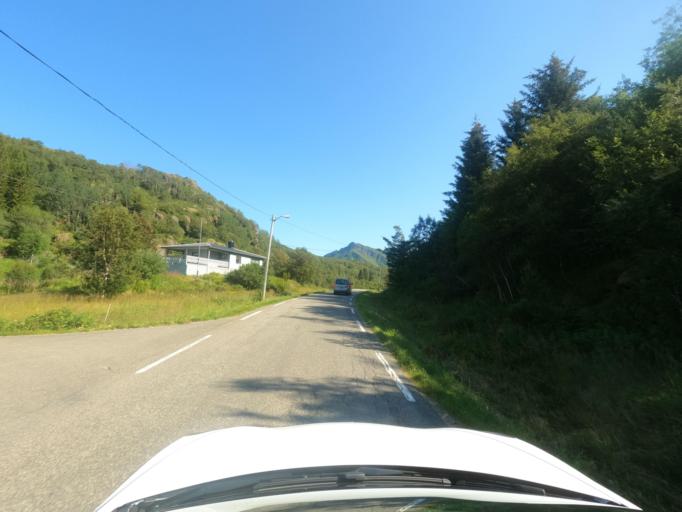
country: NO
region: Nordland
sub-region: Hadsel
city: Stokmarknes
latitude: 68.3030
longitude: 15.0273
